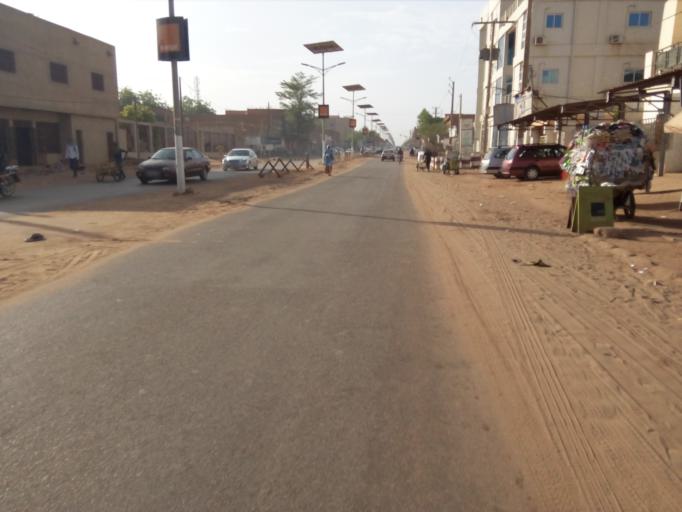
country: NE
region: Niamey
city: Niamey
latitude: 13.5152
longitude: 2.1243
